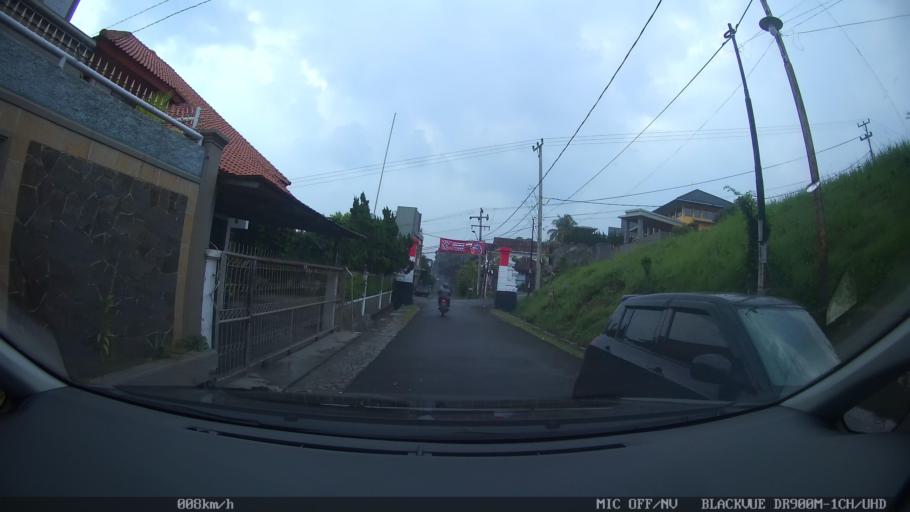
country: ID
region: Lampung
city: Bandarlampung
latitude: -5.4375
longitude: 105.2833
